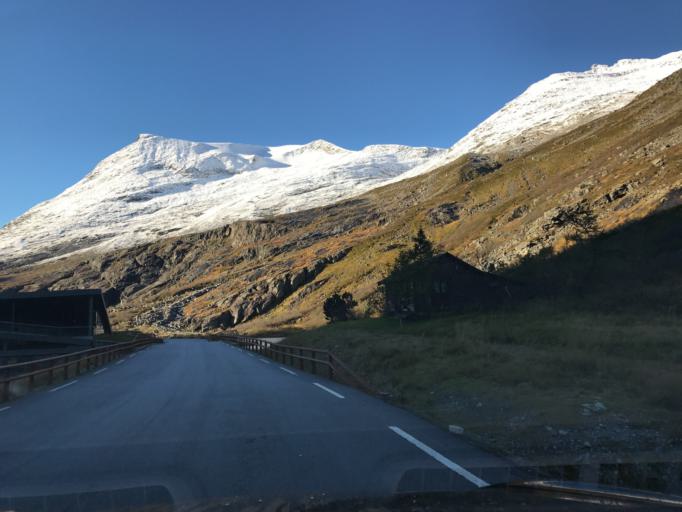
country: NO
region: More og Romsdal
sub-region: Rauma
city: Andalsnes
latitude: 62.4545
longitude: 7.6647
